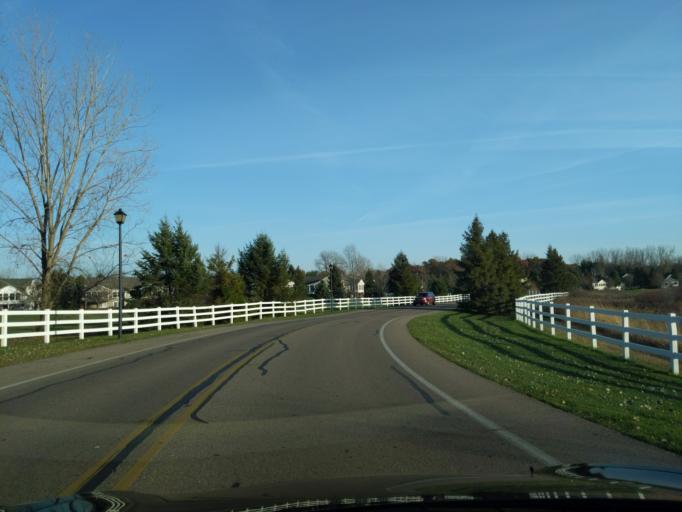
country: US
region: Michigan
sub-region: Clinton County
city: Bath
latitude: 42.7972
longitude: -84.4830
